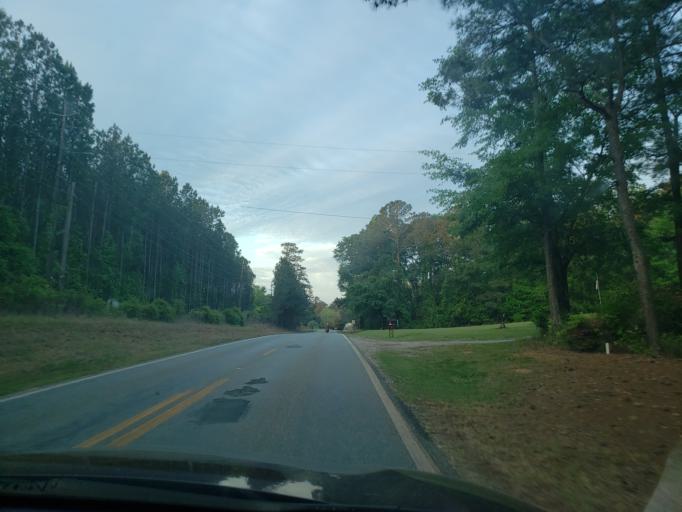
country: US
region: Alabama
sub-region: Tallapoosa County
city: Dadeville
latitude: 32.7015
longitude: -85.8425
